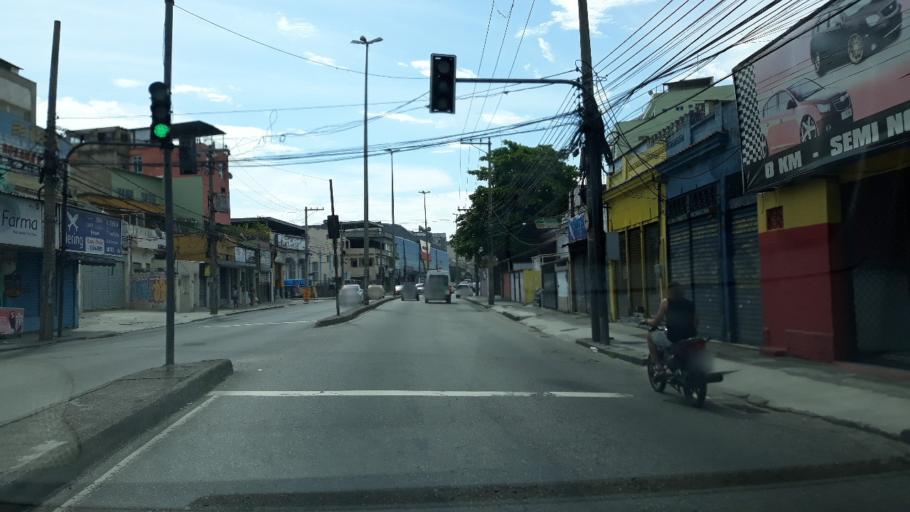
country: BR
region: Rio de Janeiro
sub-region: Rio De Janeiro
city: Rio de Janeiro
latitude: -22.8865
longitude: -43.3068
